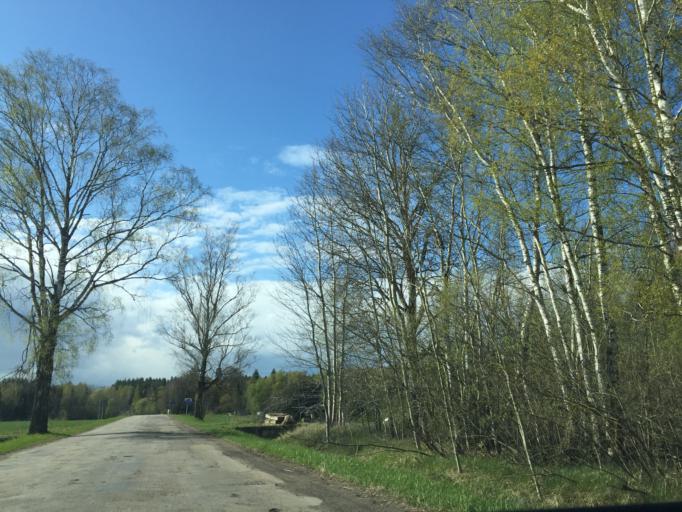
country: LV
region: Jelgava
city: Jelgava
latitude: 56.5649
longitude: 23.7586
